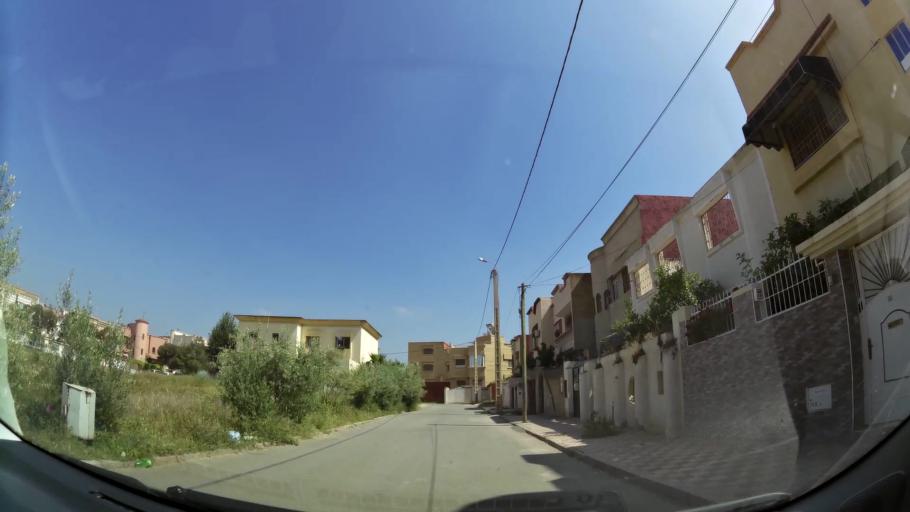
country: MA
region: Oriental
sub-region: Oujda-Angad
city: Oujda
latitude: 34.6869
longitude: -1.8745
